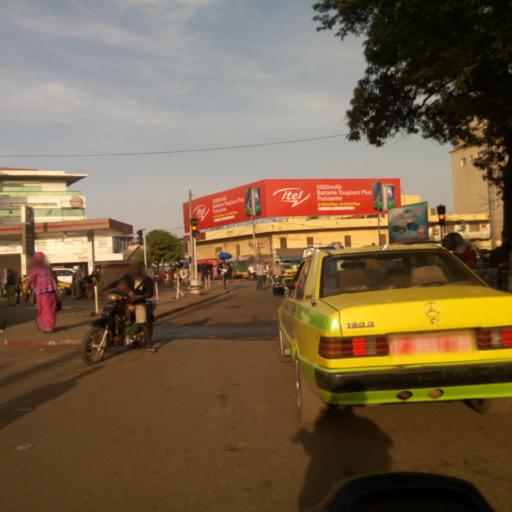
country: ML
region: Bamako
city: Bamako
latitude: 12.6442
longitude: -8.0005
